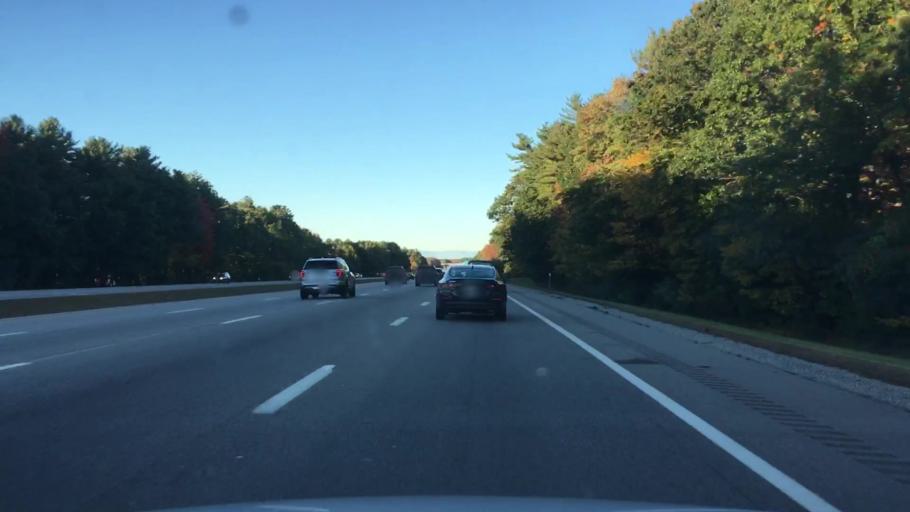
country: US
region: New Hampshire
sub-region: Rockingham County
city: Greenland
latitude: 43.0260
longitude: -70.8263
